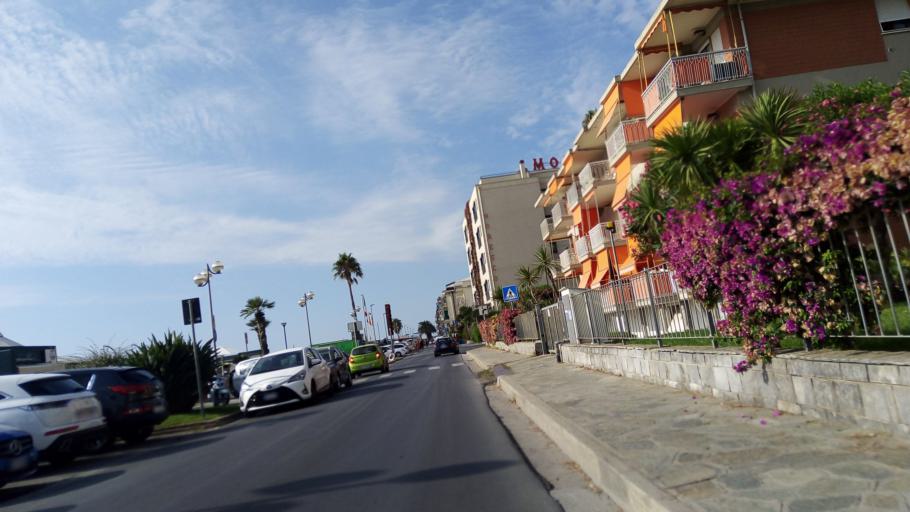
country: IT
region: Liguria
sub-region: Provincia di Savona
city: Ceriale
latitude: 44.0902
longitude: 8.2301
